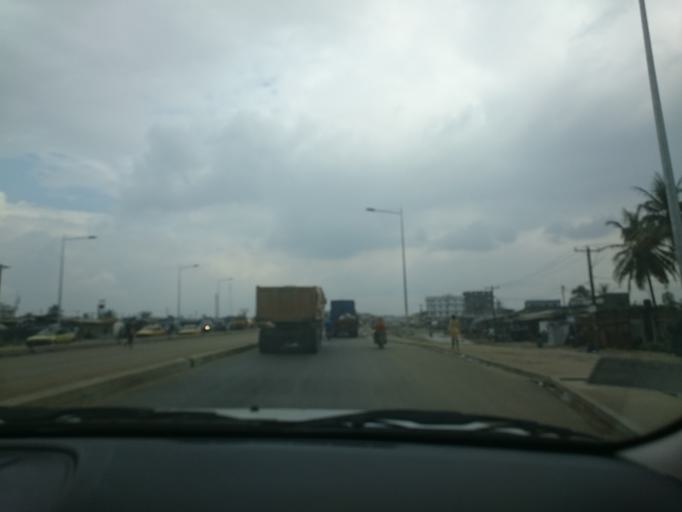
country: CM
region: Littoral
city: Douala
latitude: 4.0117
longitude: 9.7341
